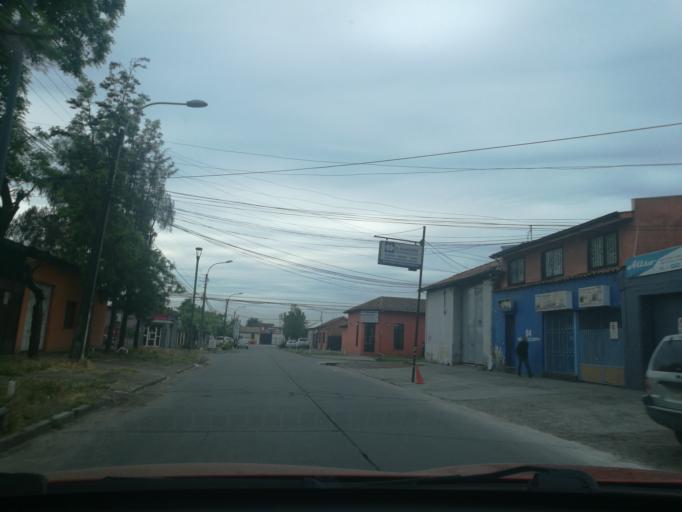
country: CL
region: O'Higgins
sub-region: Provincia de Cachapoal
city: Rancagua
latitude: -34.1648
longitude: -70.7384
